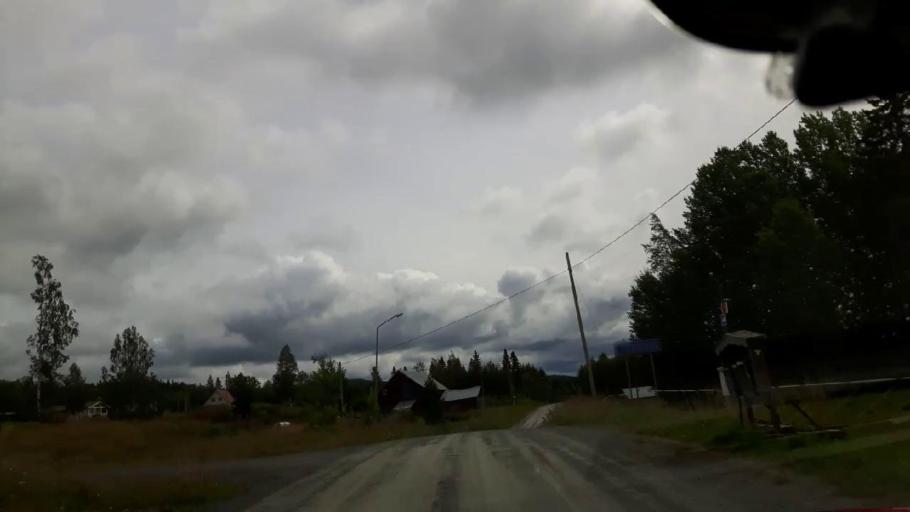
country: SE
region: Jaemtland
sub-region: Krokoms Kommun
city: Valla
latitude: 63.6708
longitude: 13.9549
